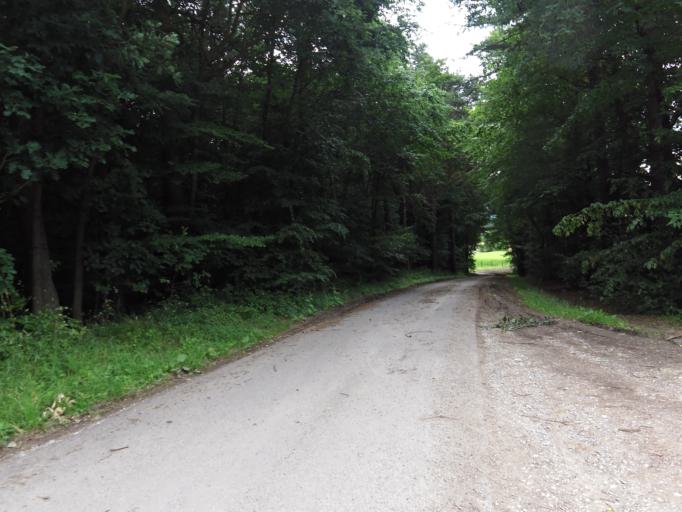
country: DE
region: Hesse
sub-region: Regierungsbezirk Kassel
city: Herleshausen
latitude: 51.0127
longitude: 10.1653
